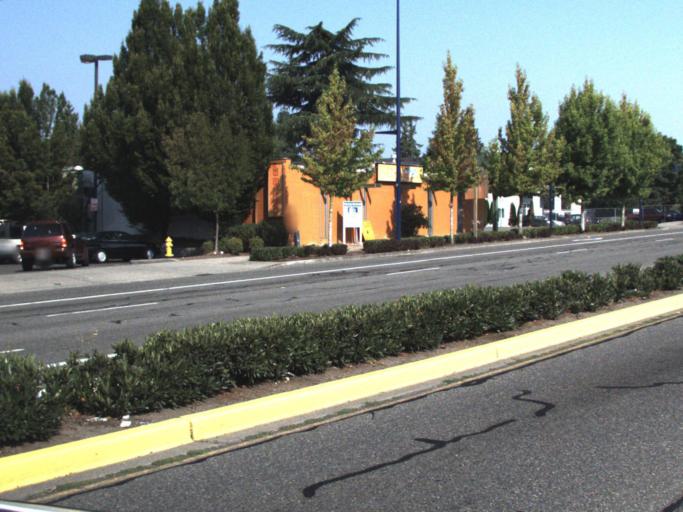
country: US
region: Washington
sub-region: King County
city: Des Moines
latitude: 47.3954
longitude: -122.2949
